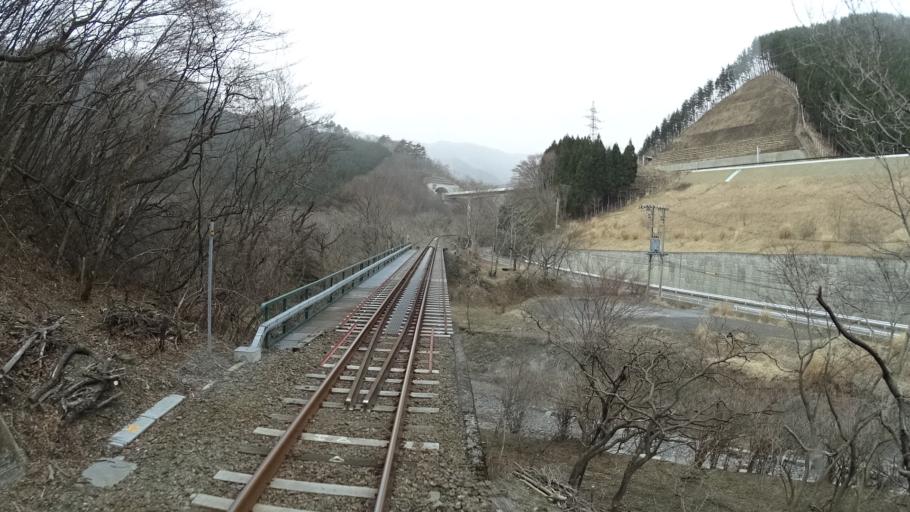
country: JP
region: Iwate
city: Kamaishi
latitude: 39.2972
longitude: 141.8686
